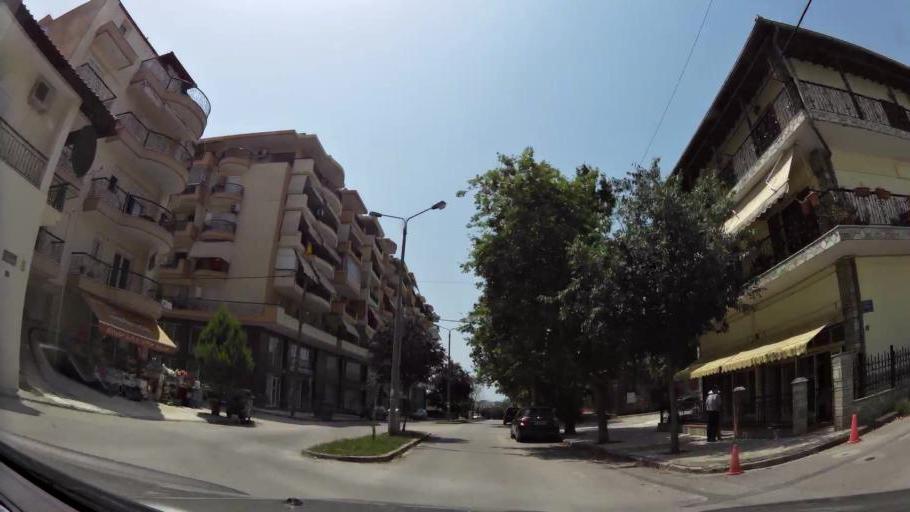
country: GR
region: Central Macedonia
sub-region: Nomos Thessalonikis
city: Evosmos
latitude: 40.6745
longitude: 22.8996
